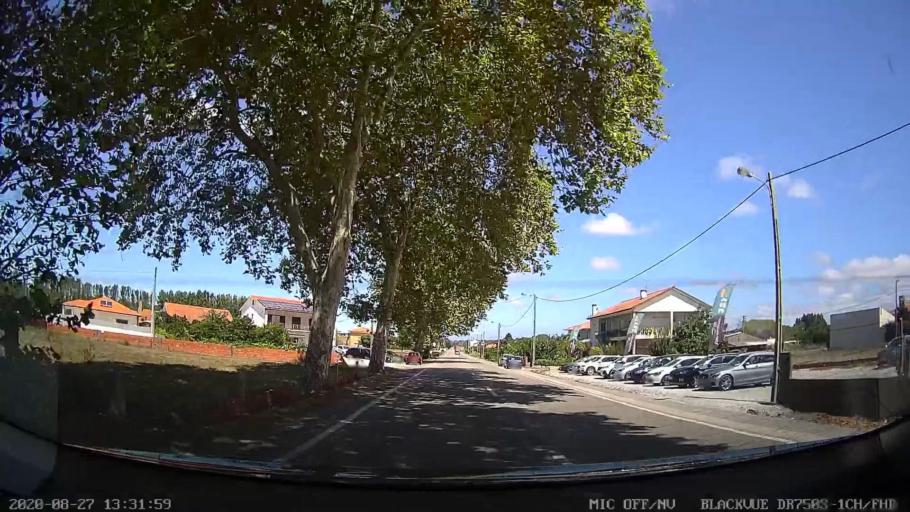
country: PT
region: Aveiro
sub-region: Vagos
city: Vagos
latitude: 40.4912
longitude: -8.6859
